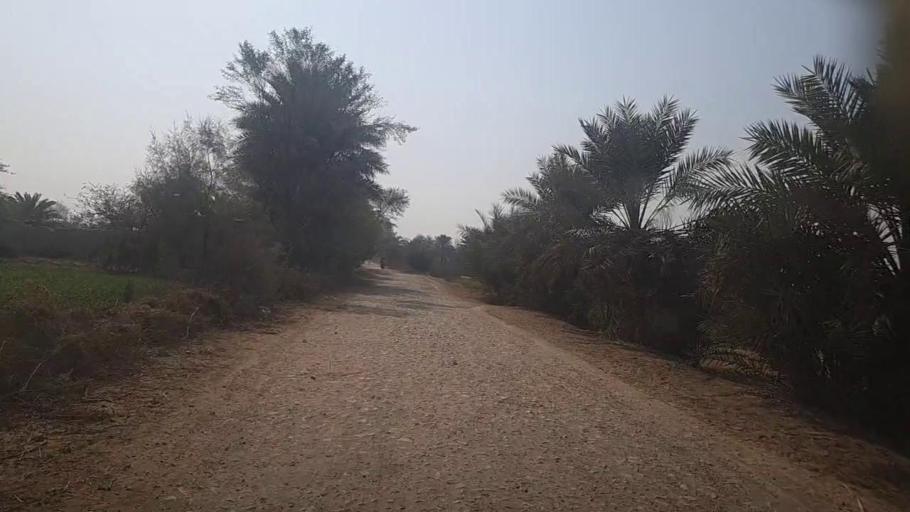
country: PK
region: Sindh
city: Kot Diji
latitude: 27.3621
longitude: 68.7436
